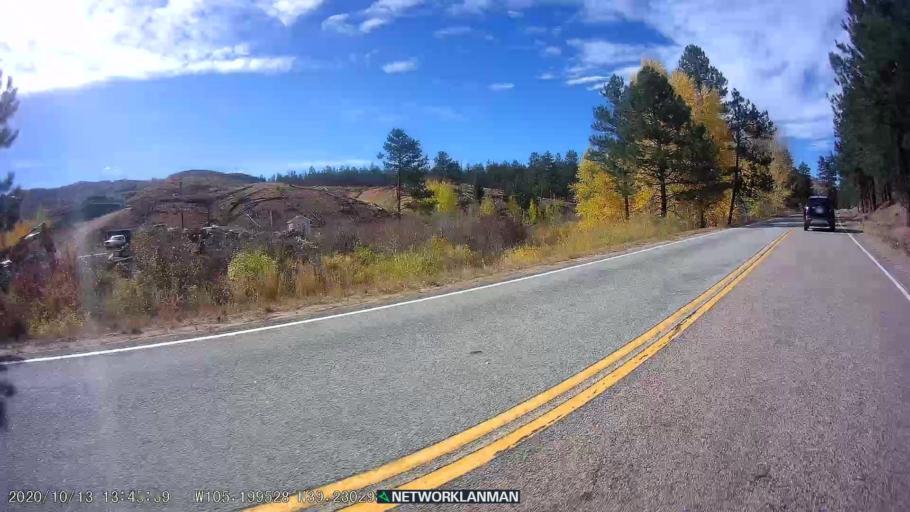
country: US
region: Colorado
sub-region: Douglas County
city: Perry Park
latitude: 39.2305
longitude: -105.1996
